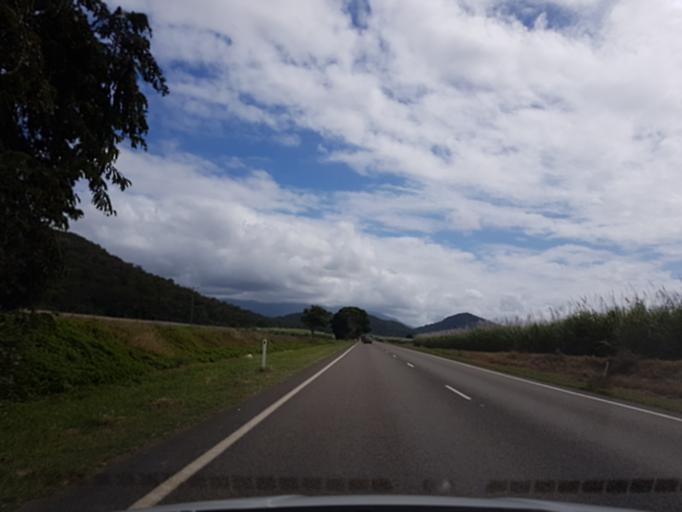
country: AU
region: Queensland
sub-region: Cairns
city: Port Douglas
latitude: -16.4852
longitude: 145.4133
